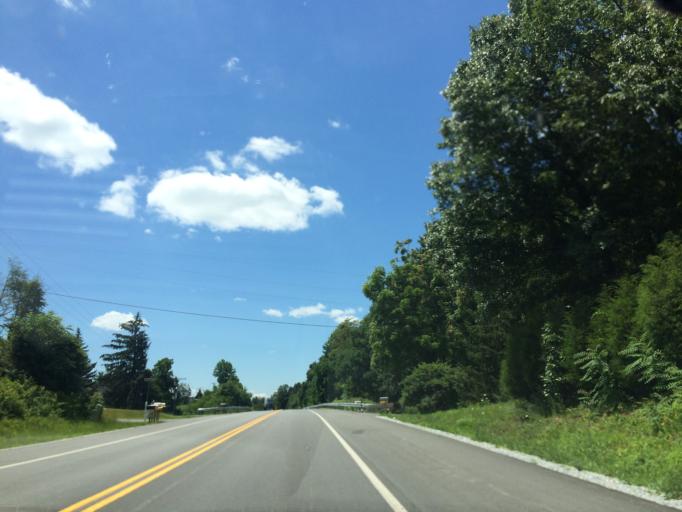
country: US
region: Maryland
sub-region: Carroll County
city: New Windsor
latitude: 39.4622
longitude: -77.1102
